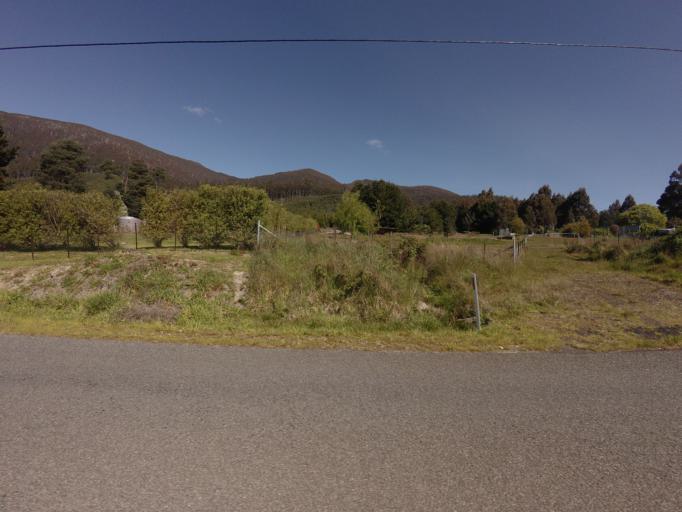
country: AU
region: Tasmania
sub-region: Derwent Valley
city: New Norfolk
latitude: -42.7499
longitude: 146.6439
